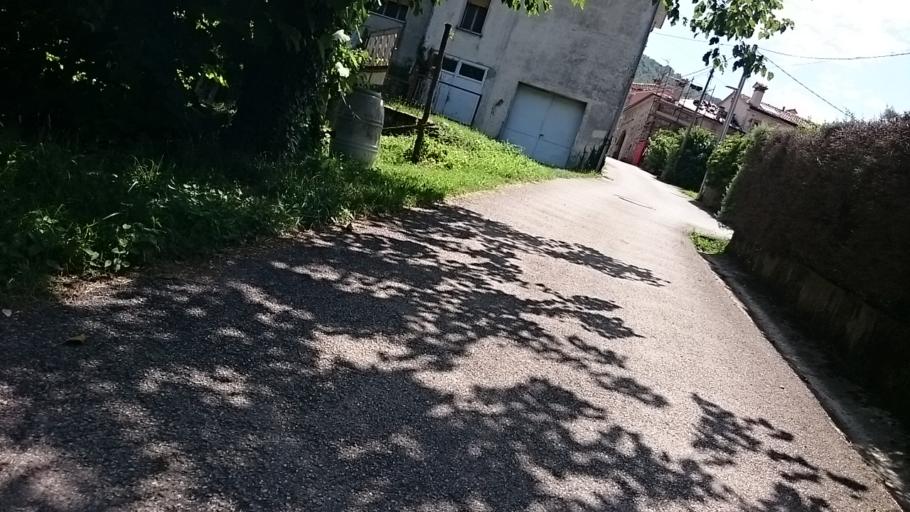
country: IT
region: Veneto
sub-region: Provincia di Treviso
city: Santa Maria
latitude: 45.9862
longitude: 12.2336
